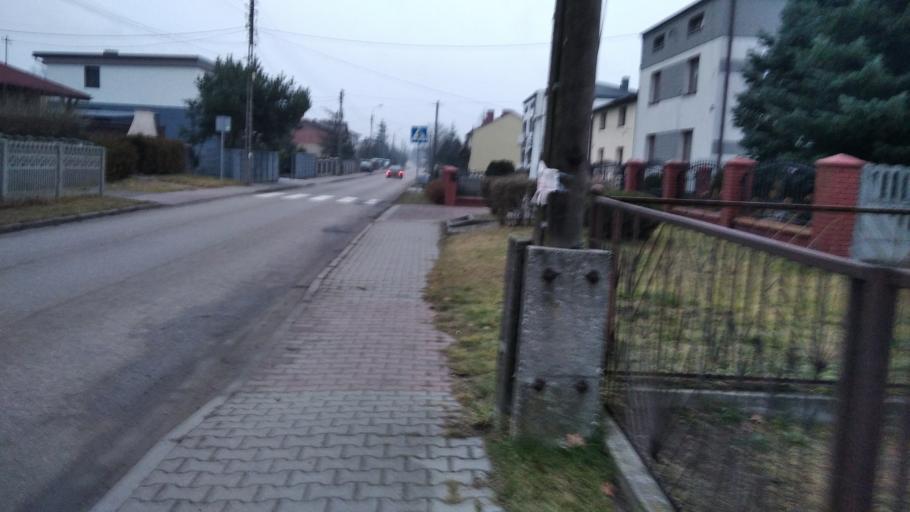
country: PL
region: Silesian Voivodeship
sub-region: Powiat bedzinski
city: Psary
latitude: 50.4014
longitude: 19.1281
